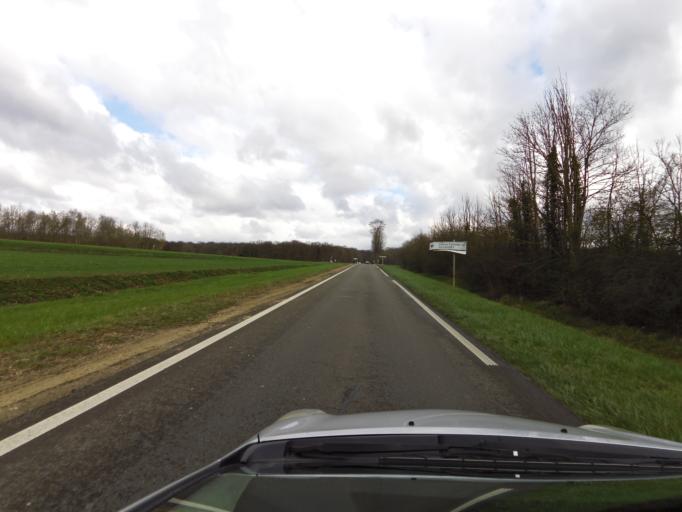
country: FR
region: Picardie
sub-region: Departement de l'Oise
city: Chamant
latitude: 49.2249
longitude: 2.5906
